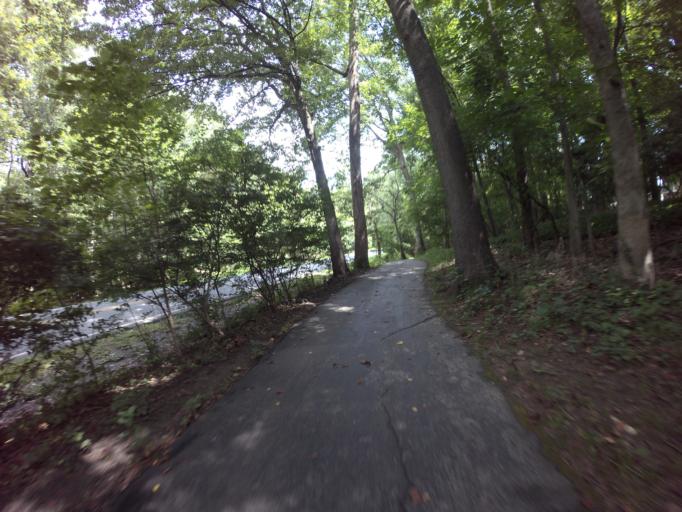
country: US
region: Maryland
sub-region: Montgomery County
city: Kensington
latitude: 39.0290
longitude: -77.0876
